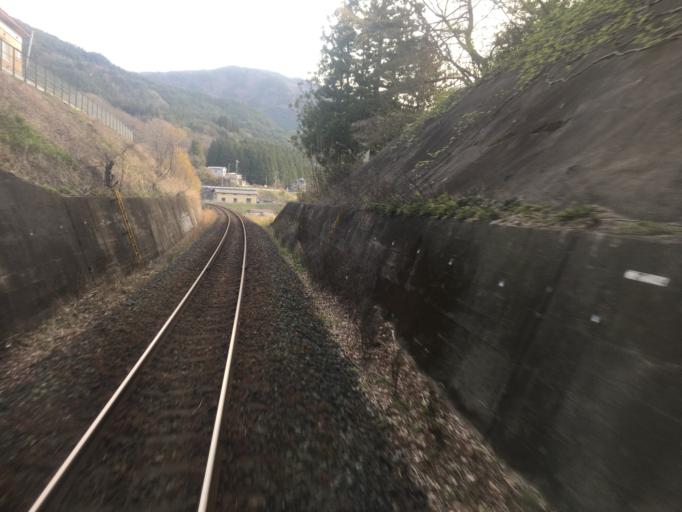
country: JP
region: Iwate
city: Kamaishi
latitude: 39.1548
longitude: 141.8434
